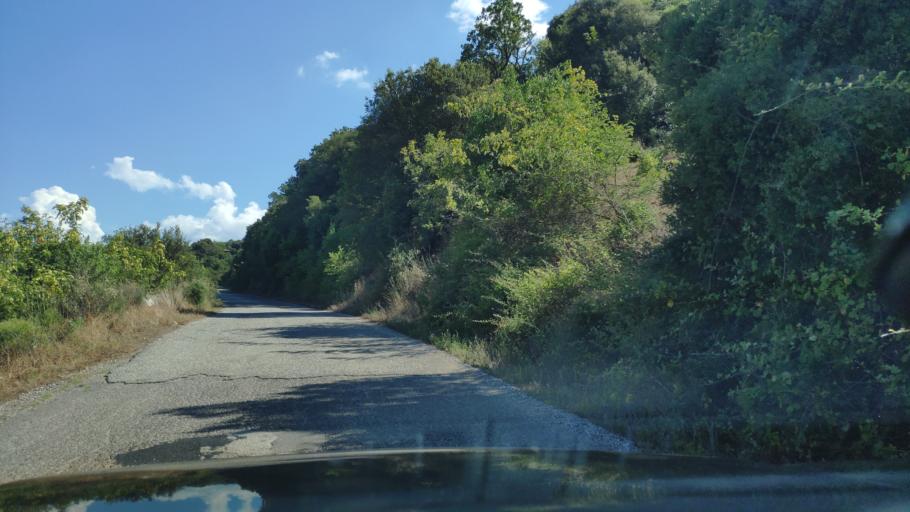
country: GR
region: West Greece
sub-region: Nomos Aitolias kai Akarnanias
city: Katouna
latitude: 38.8200
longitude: 21.1031
